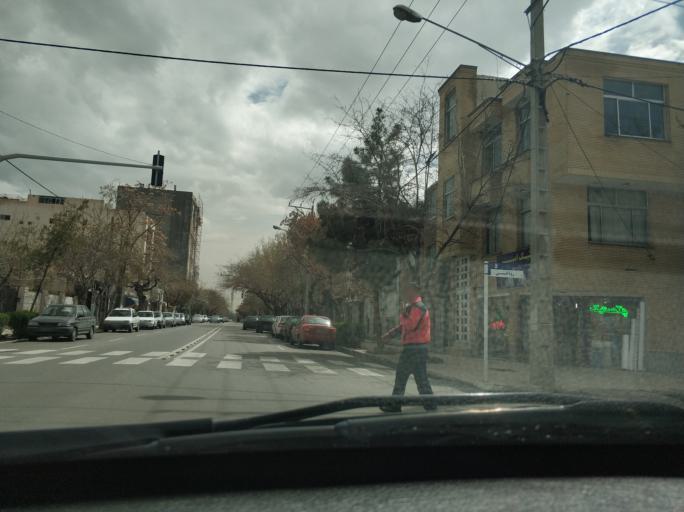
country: IR
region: Razavi Khorasan
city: Mashhad
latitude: 36.2804
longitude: 59.5736
